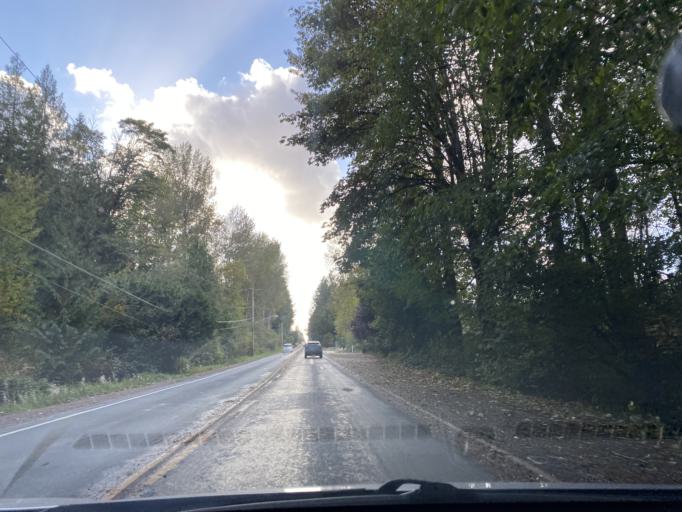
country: US
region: Washington
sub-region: Pierce County
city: South Hill
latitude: 47.1185
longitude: -122.2721
